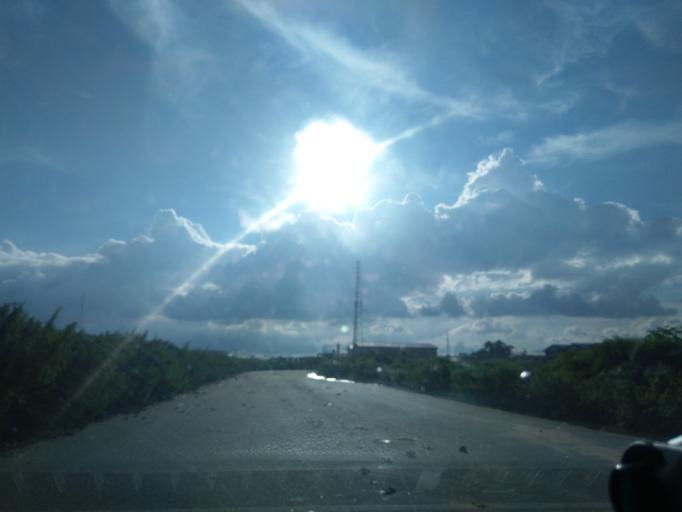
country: NG
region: Abuja Federal Capital Territory
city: Abuja
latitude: 9.0296
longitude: 7.4060
